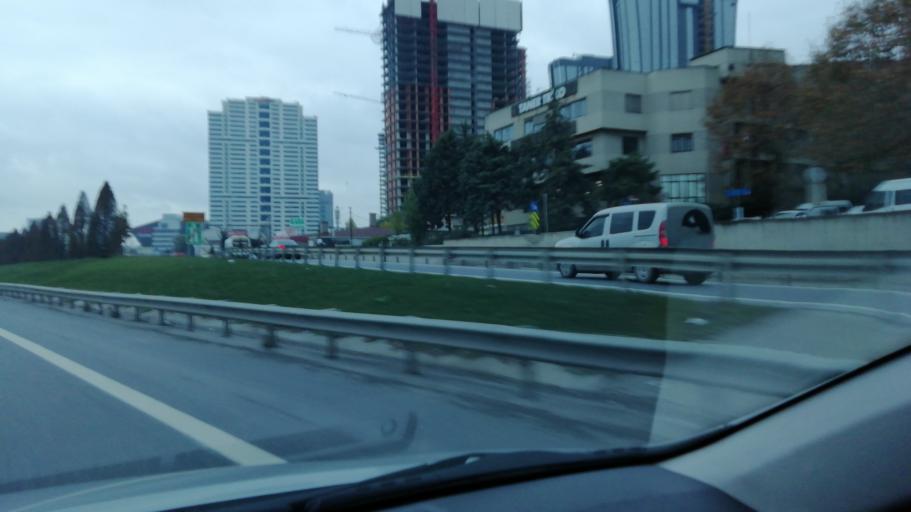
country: TR
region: Istanbul
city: Mahmutbey
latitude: 41.0419
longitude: 28.8093
